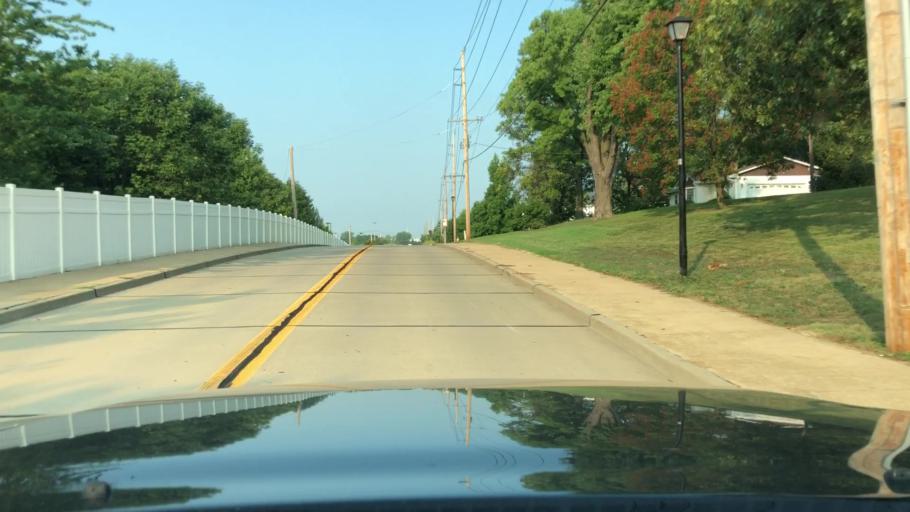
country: US
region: Missouri
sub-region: Saint Charles County
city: Saint Peters
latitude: 38.8026
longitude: -90.5601
